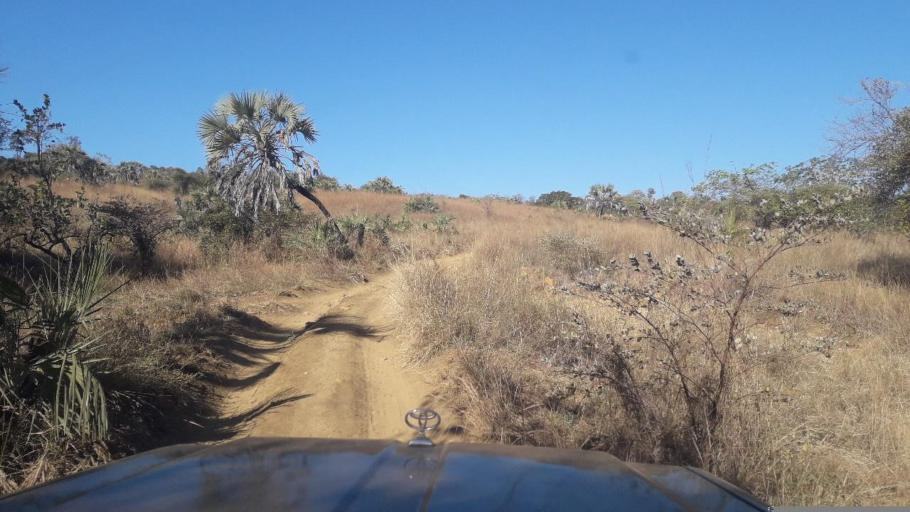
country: MG
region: Boeny
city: Sitampiky
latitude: -16.3976
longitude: 45.5959
